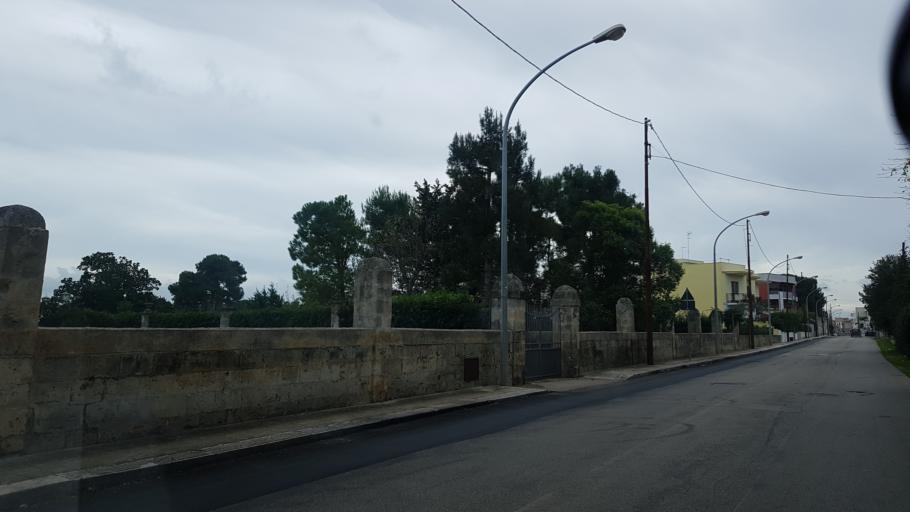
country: IT
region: Apulia
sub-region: Provincia di Brindisi
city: Mesagne
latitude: 40.5668
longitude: 17.8012
